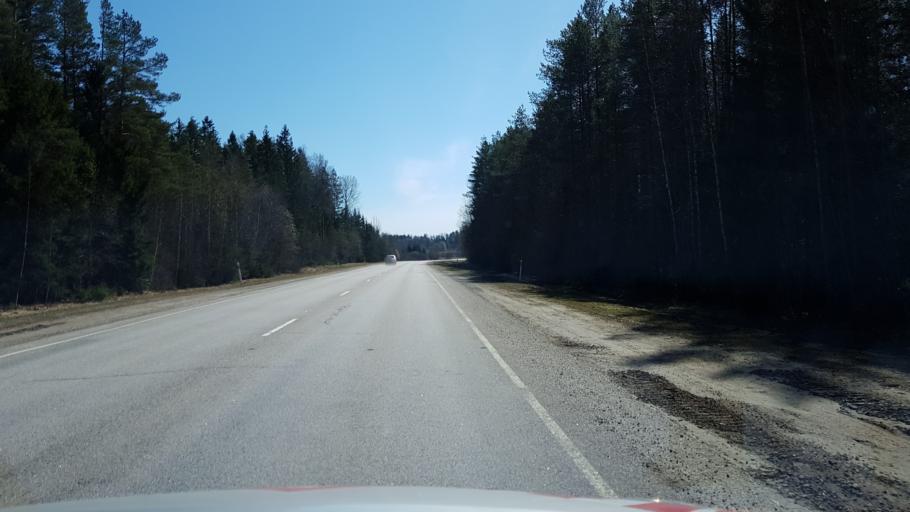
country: EE
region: Ida-Virumaa
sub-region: Johvi vald
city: Johvi
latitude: 59.1557
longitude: 27.3575
